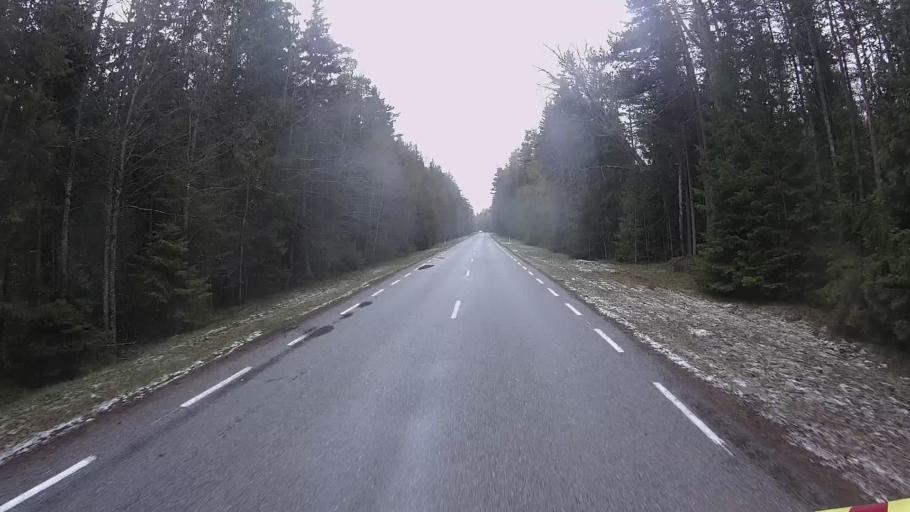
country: EE
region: Hiiumaa
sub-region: Kaerdla linn
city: Kardla
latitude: 59.0582
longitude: 22.6834
